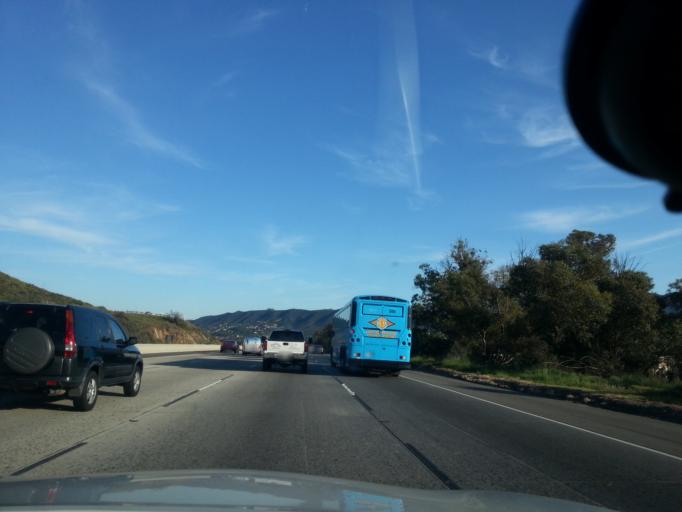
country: US
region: California
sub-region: Ventura County
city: Casa Conejo
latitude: 34.1964
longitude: -118.9517
